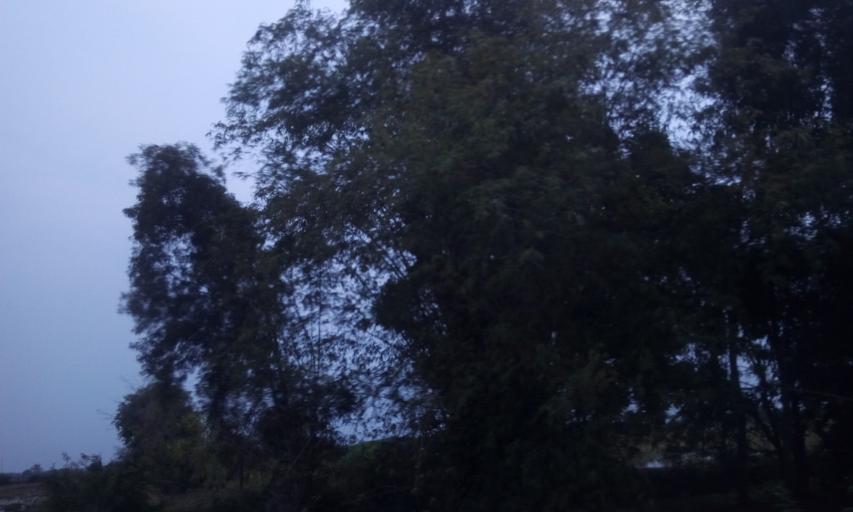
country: TH
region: Chachoengsao
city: Plaeng Yao
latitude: 13.5919
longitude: 101.2002
